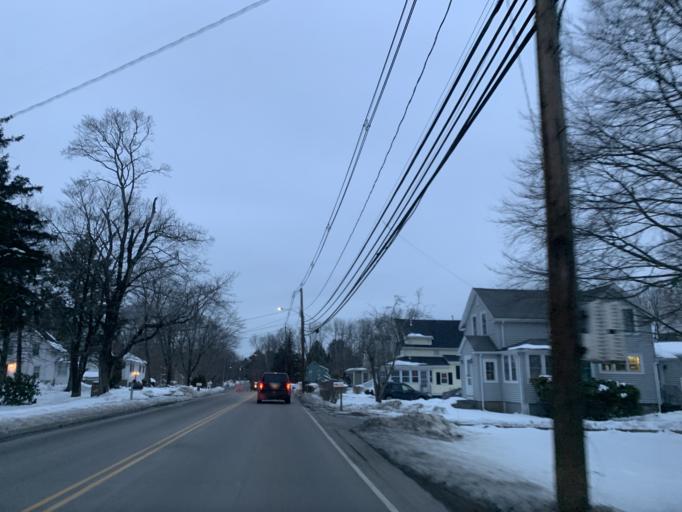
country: US
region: Massachusetts
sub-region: Norfolk County
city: Canton
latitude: 42.1492
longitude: -71.1236
